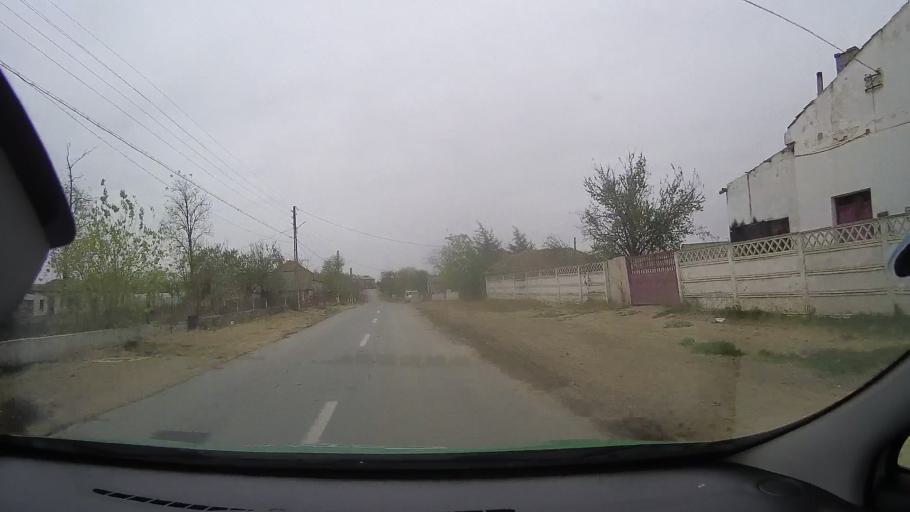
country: RO
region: Constanta
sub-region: Comuna Vulturu
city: Vulturu
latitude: 44.6448
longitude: 28.2715
